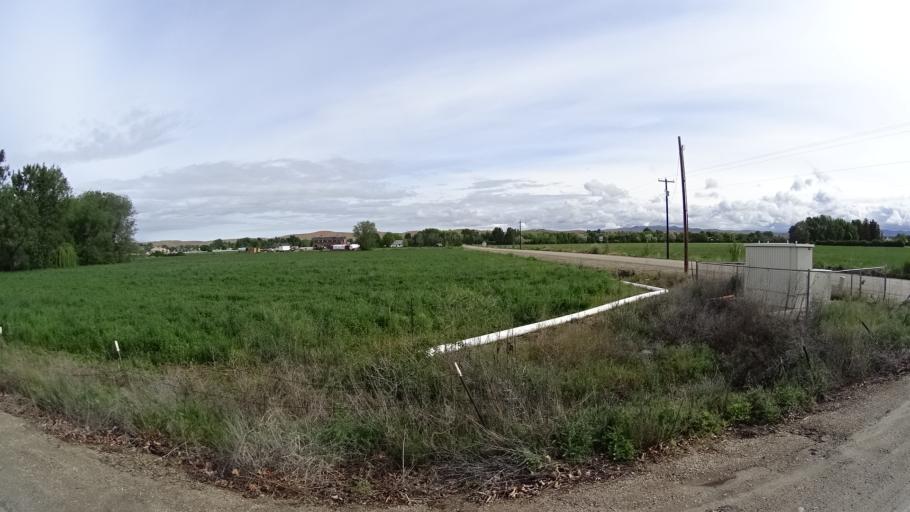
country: US
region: Idaho
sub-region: Ada County
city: Eagle
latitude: 43.7209
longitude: -116.4037
